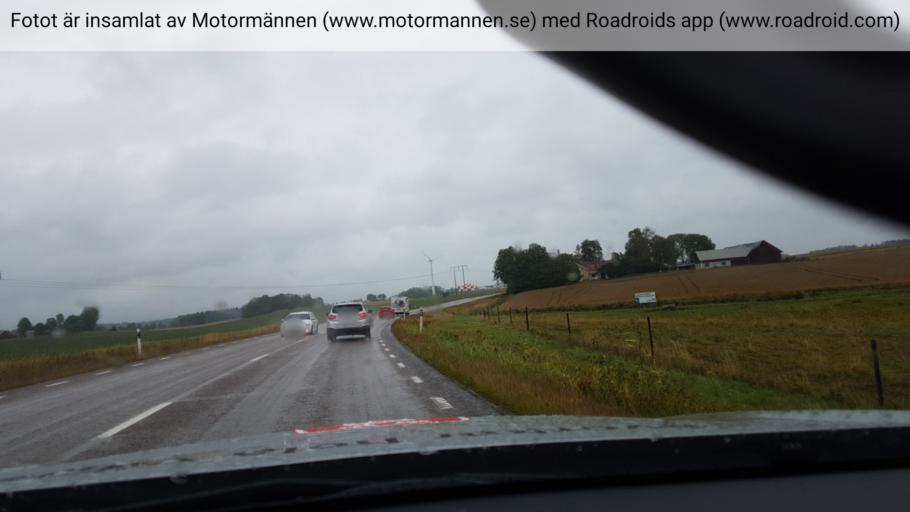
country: SE
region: Vaestra Goetaland
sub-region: Melleruds Kommun
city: Mellerud
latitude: 58.7246
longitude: 12.4534
